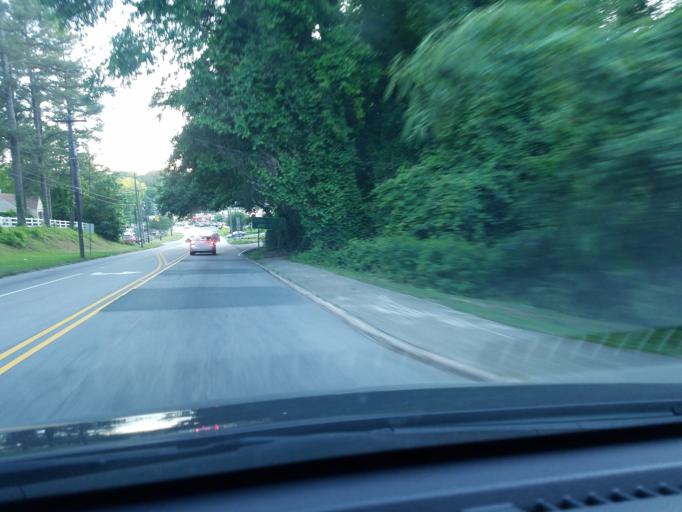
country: US
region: North Carolina
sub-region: Durham County
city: Durham
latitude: 35.9757
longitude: -78.9222
